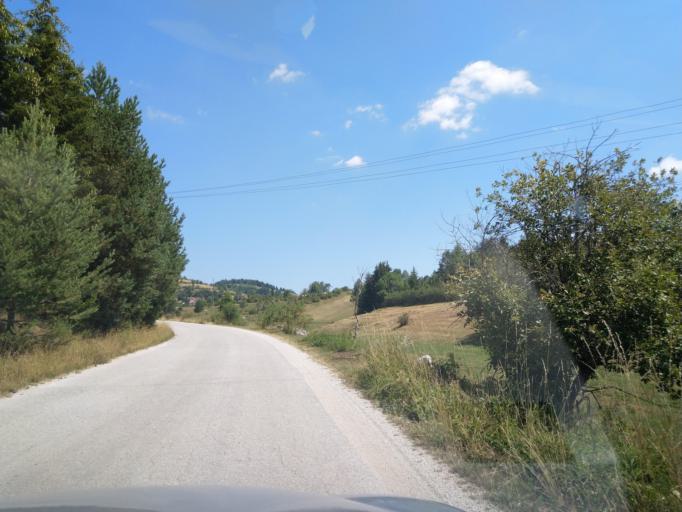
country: RS
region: Central Serbia
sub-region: Zlatiborski Okrug
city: Nova Varos
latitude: 43.4490
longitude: 19.9672
